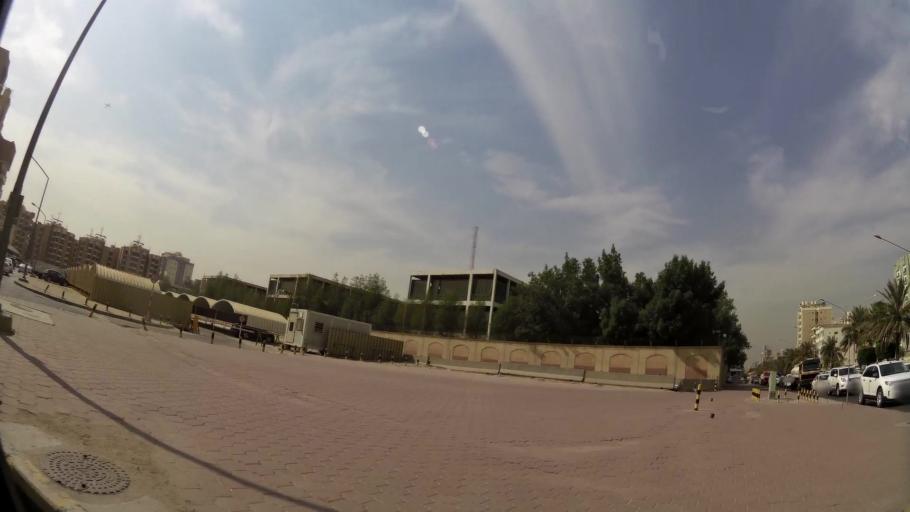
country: KW
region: Al Farwaniyah
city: Al Farwaniyah
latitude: 29.2825
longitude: 47.9721
